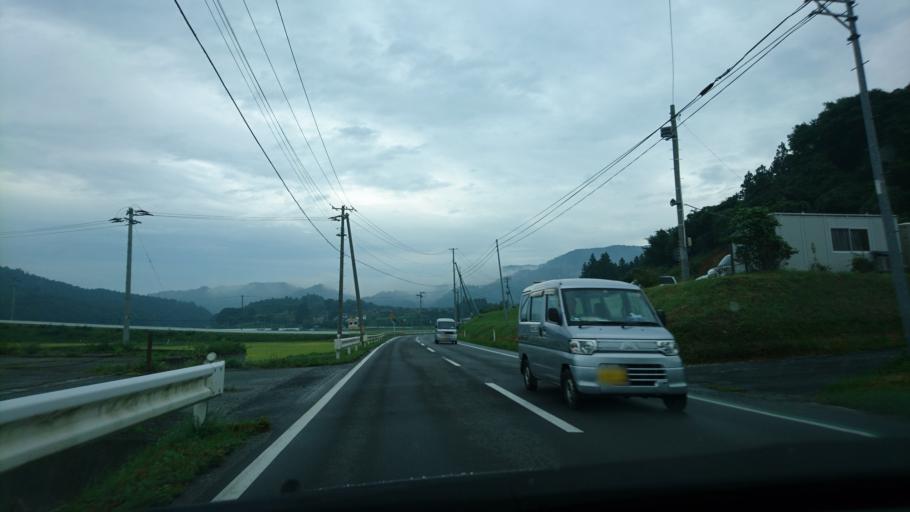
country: JP
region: Iwate
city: Ichinoseki
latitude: 38.9450
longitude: 141.2510
